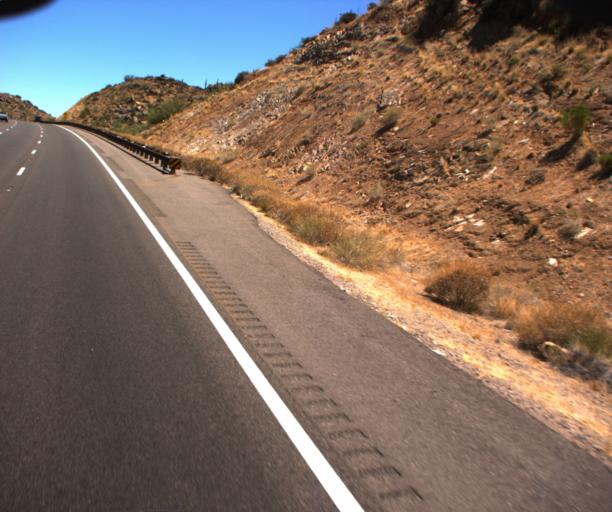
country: US
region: Arizona
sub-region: Maricopa County
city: Rio Verde
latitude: 33.7030
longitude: -111.5048
